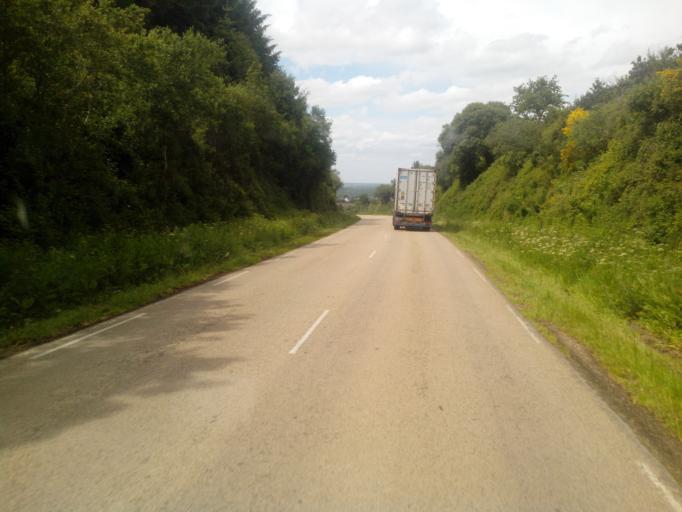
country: FR
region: Brittany
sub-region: Departement du Finistere
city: Guerlesquin
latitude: 48.5602
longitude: -3.6002
